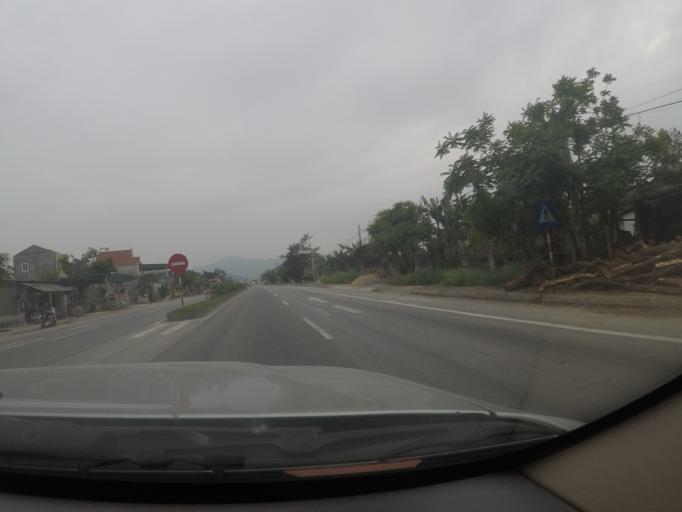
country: VN
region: Nghe An
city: Dien Chau
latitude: 18.9196
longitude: 105.6087
